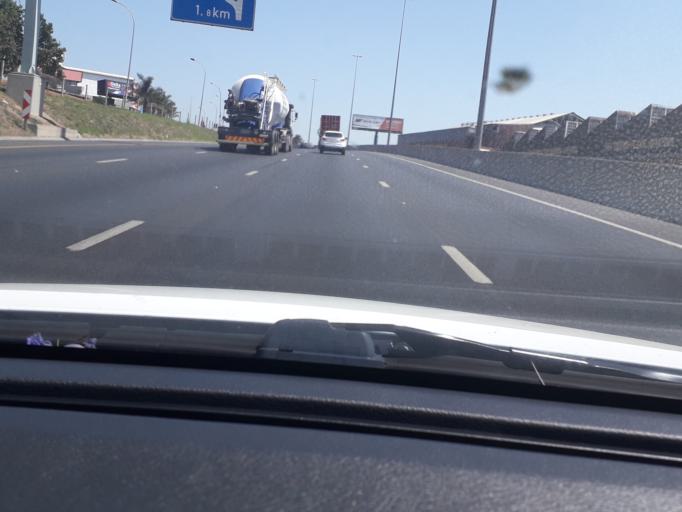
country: ZA
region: Gauteng
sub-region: Ekurhuleni Metropolitan Municipality
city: Germiston
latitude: -26.1692
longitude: 28.1912
